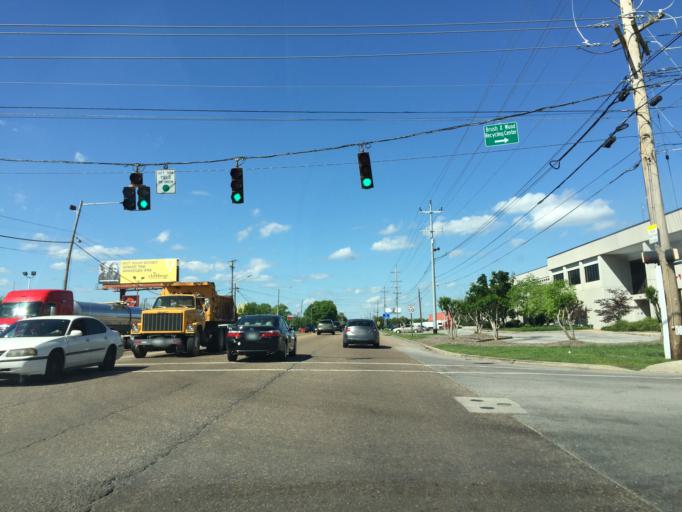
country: US
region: Tennessee
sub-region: Hamilton County
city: East Chattanooga
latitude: 35.0811
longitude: -85.2642
